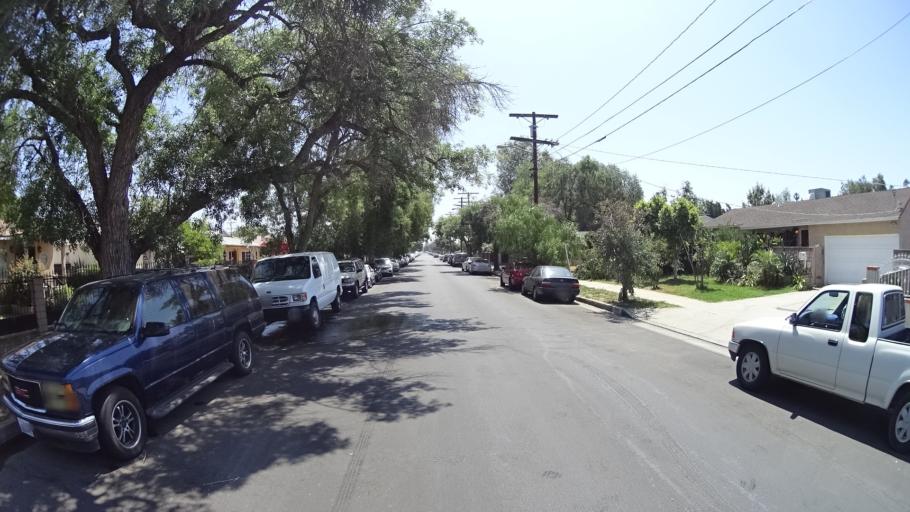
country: US
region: California
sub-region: Los Angeles County
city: Van Nuys
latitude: 34.2067
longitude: -118.4569
